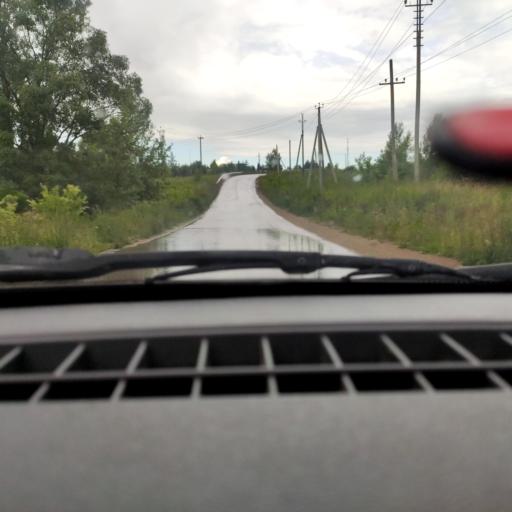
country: RU
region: Bashkortostan
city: Kabakovo
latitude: 54.5655
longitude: 56.2710
